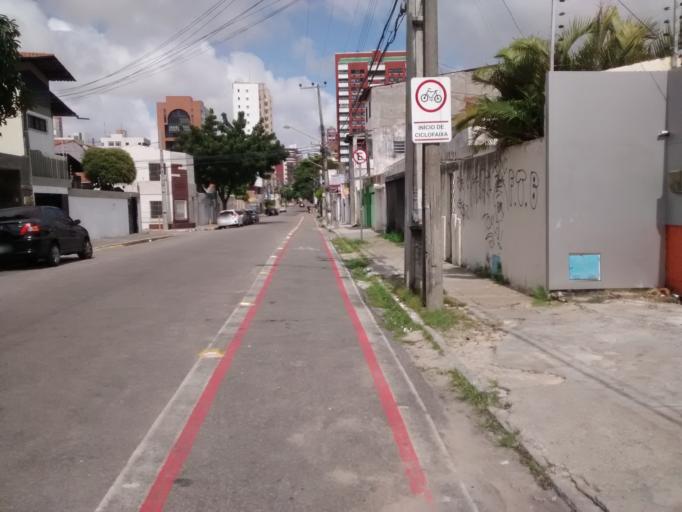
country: BR
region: Ceara
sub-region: Fortaleza
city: Fortaleza
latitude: -3.7314
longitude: -38.4852
